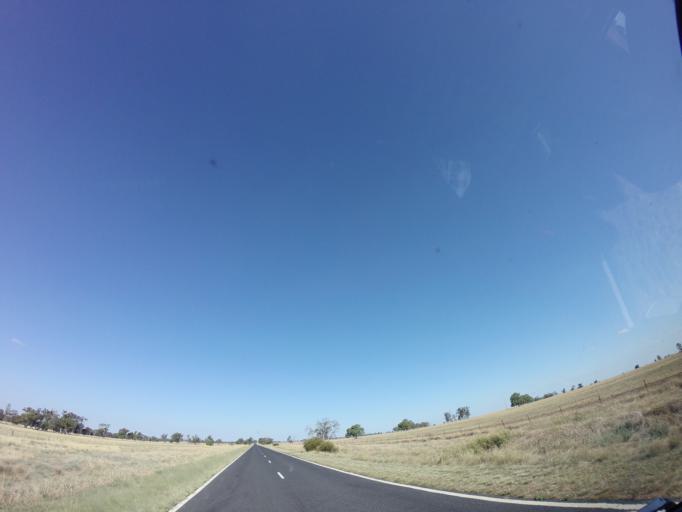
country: AU
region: New South Wales
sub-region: Gilgandra
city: Gilgandra
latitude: -31.6626
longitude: 148.3745
